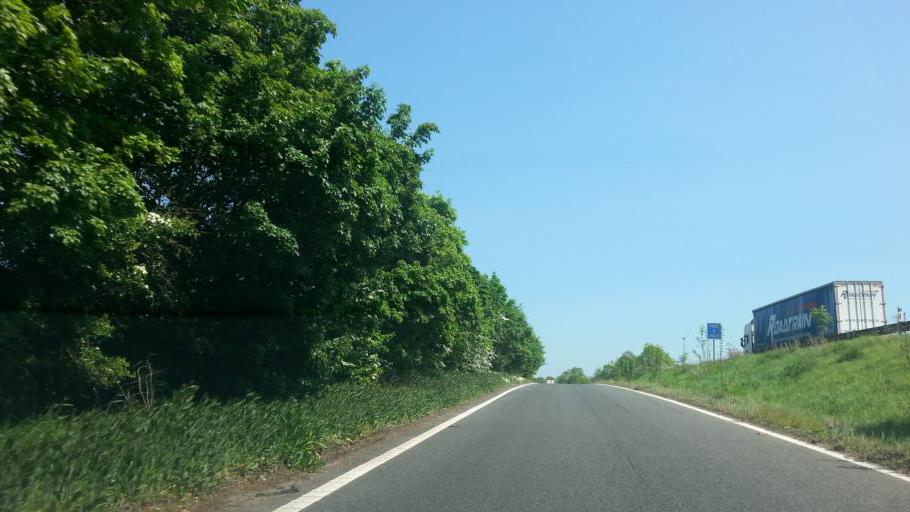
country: GB
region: England
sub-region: Leicestershire
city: Hinckley
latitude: 52.5162
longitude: -1.3583
